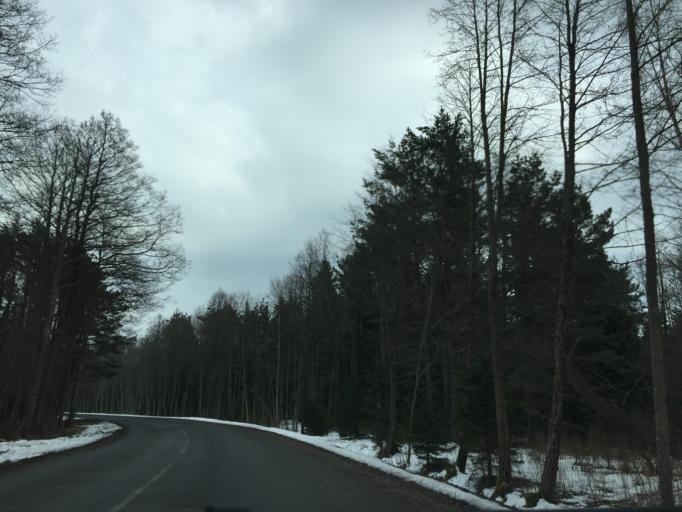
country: EE
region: Saare
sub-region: Kuressaare linn
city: Kuressaare
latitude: 58.4165
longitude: 22.0783
